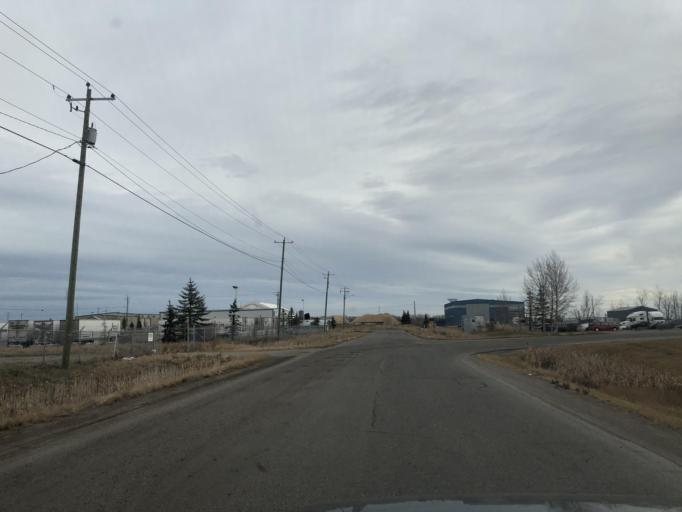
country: CA
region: Alberta
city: Chestermere
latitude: 50.9833
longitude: -113.9041
